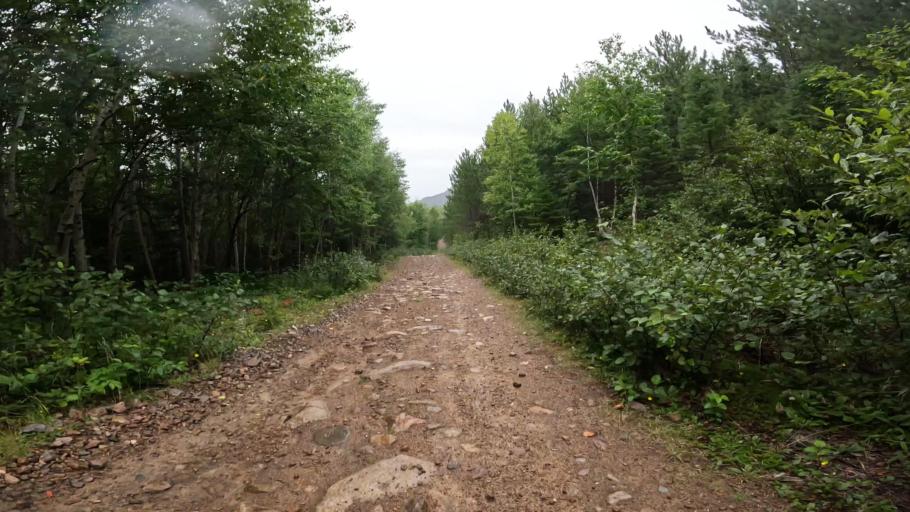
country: CA
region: Quebec
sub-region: Capitale-Nationale
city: Baie-Saint-Paul
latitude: 47.7927
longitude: -70.4882
